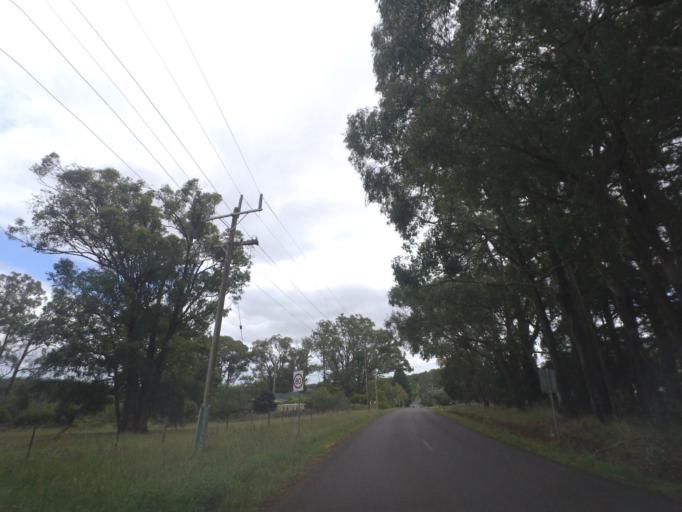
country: AU
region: Victoria
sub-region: Yarra Ranges
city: Launching Place
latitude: -37.8378
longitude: 145.5861
